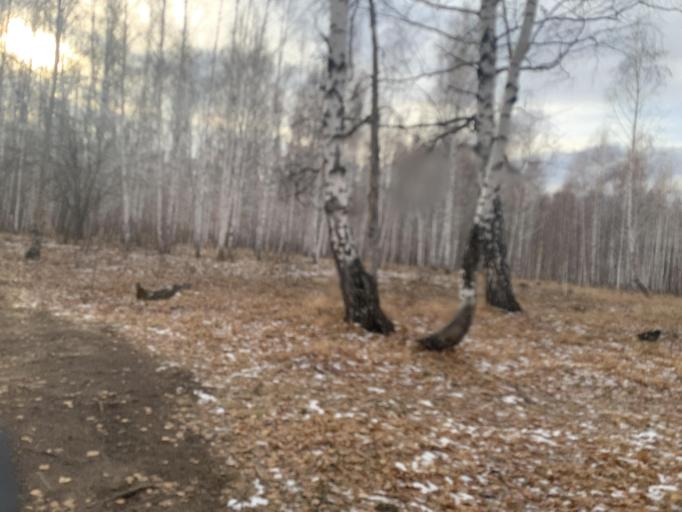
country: RU
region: Chelyabinsk
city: Roshchino
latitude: 55.2024
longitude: 61.3033
